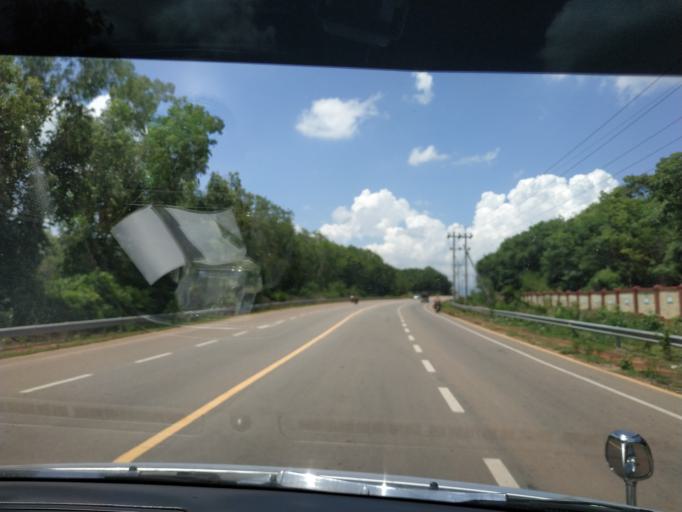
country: MM
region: Mon
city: Kyaikto
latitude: 17.3215
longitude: 97.0216
